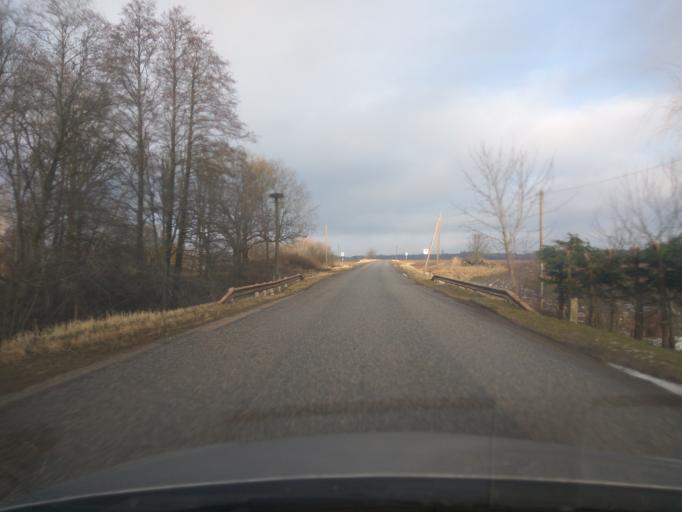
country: LV
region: Saldus Rajons
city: Saldus
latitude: 56.7627
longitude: 22.3856
